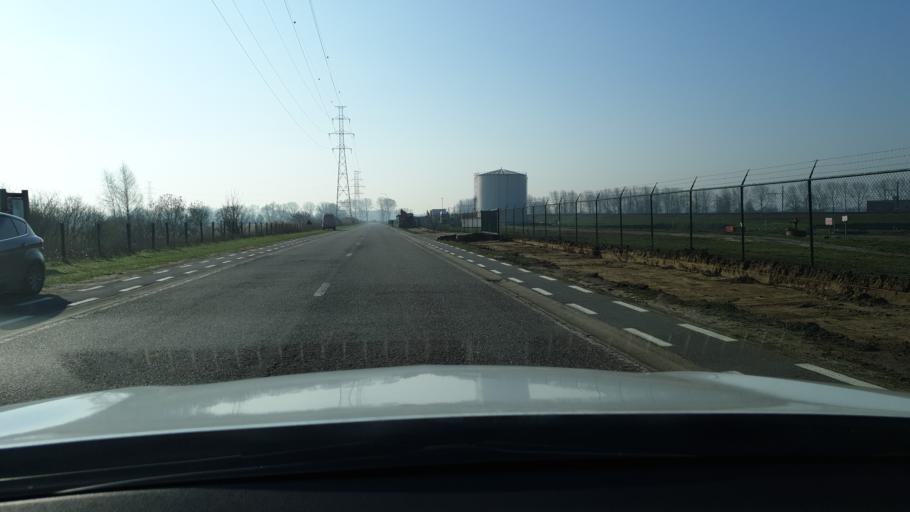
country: BE
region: Flanders
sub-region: Provincie Antwerpen
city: Zwijndrecht
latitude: 51.2441
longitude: 4.2888
